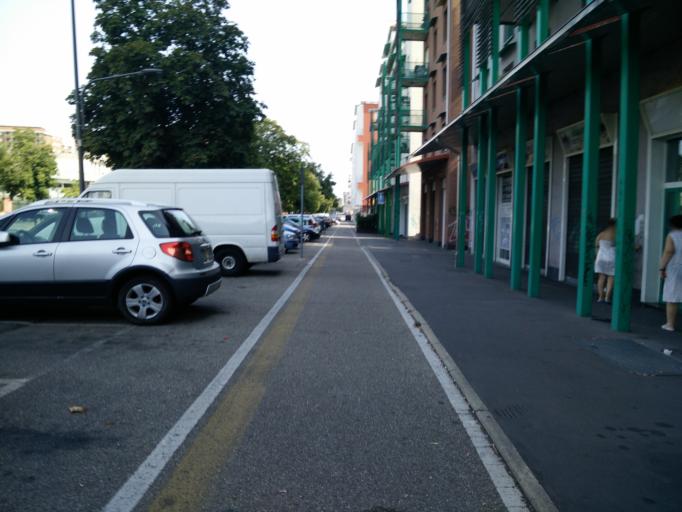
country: IT
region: Piedmont
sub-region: Provincia di Torino
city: Nichelino
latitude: 45.0279
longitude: 7.6540
